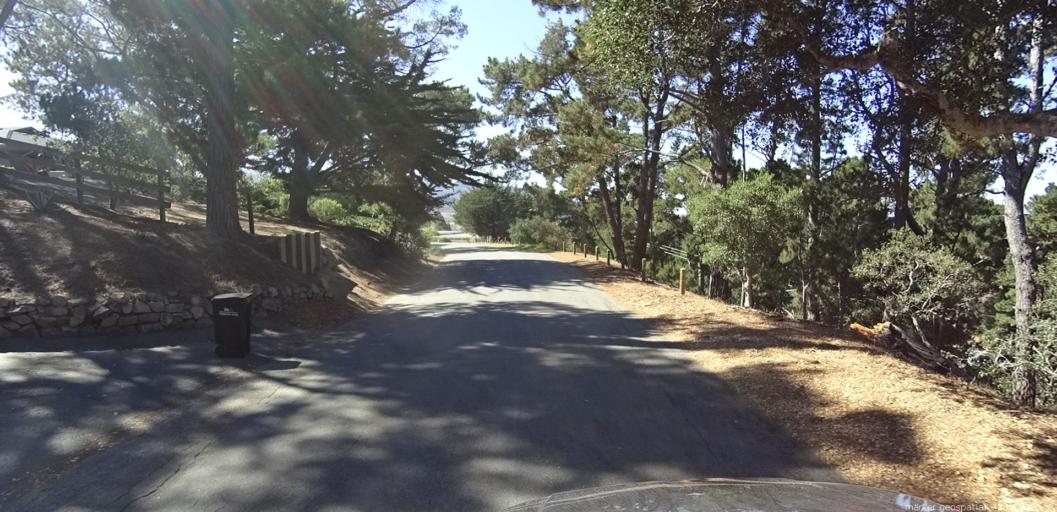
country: US
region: California
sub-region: Monterey County
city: Carmel-by-the-Sea
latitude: 36.5486
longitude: -121.9027
